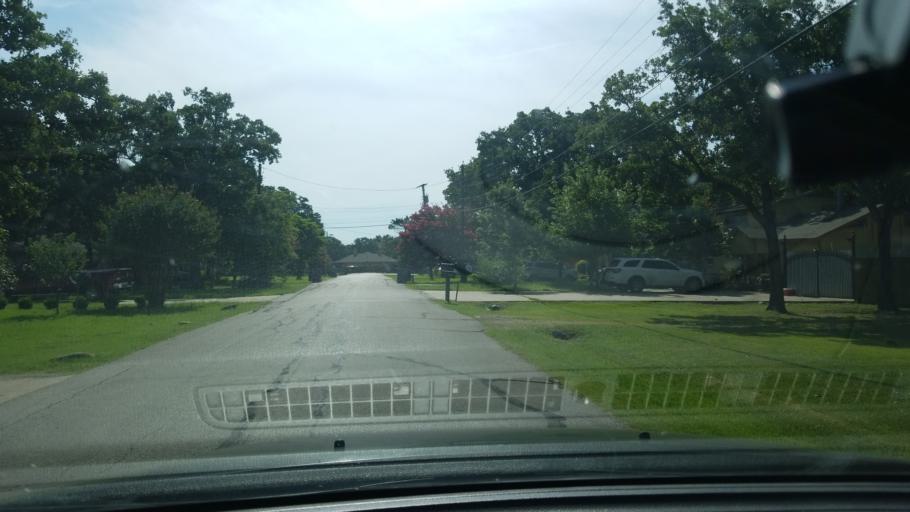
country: US
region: Texas
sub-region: Dallas County
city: Balch Springs
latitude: 32.7296
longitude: -96.6375
